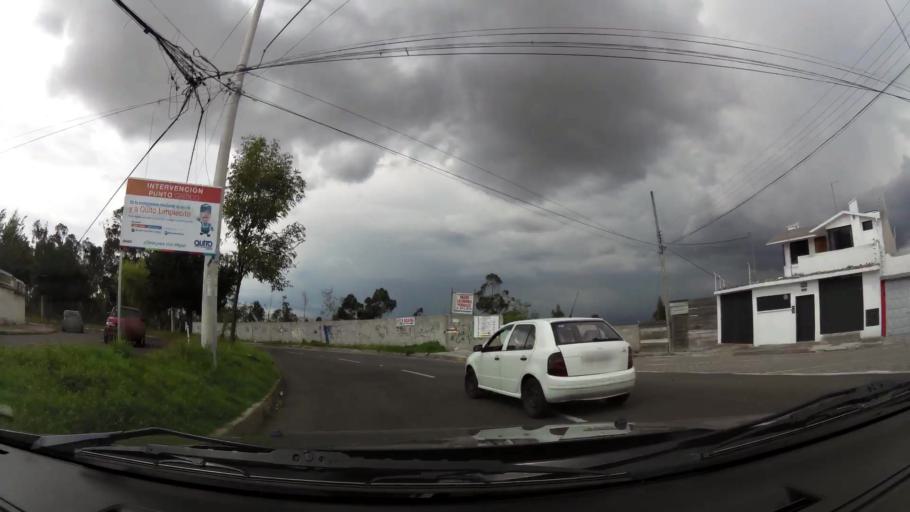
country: EC
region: Pichincha
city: Quito
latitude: -0.0915
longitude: -78.4676
